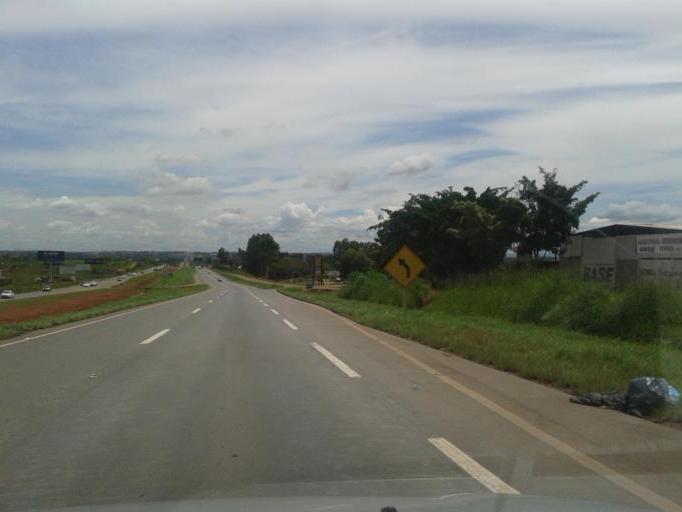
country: BR
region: Goias
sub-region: Aparecida De Goiania
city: Aparecida de Goiania
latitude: -16.8914
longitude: -49.2550
